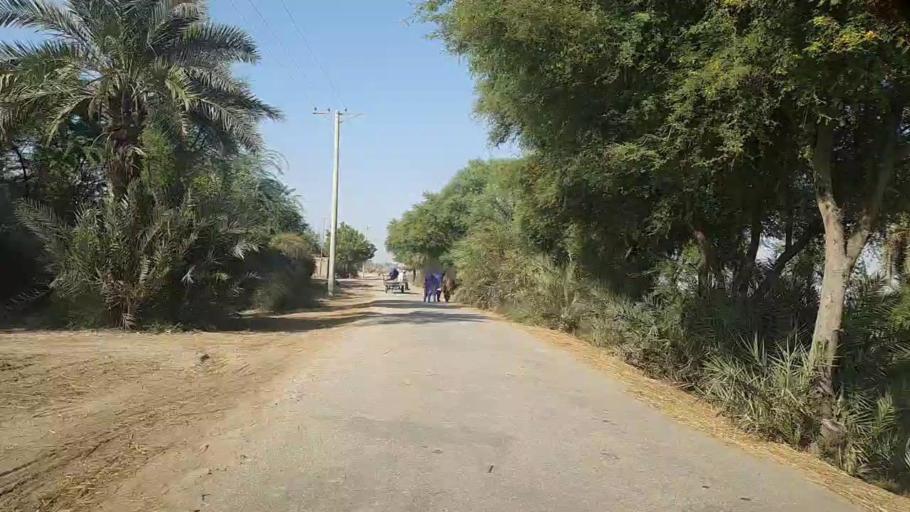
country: PK
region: Sindh
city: Tangwani
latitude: 28.2464
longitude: 68.9963
